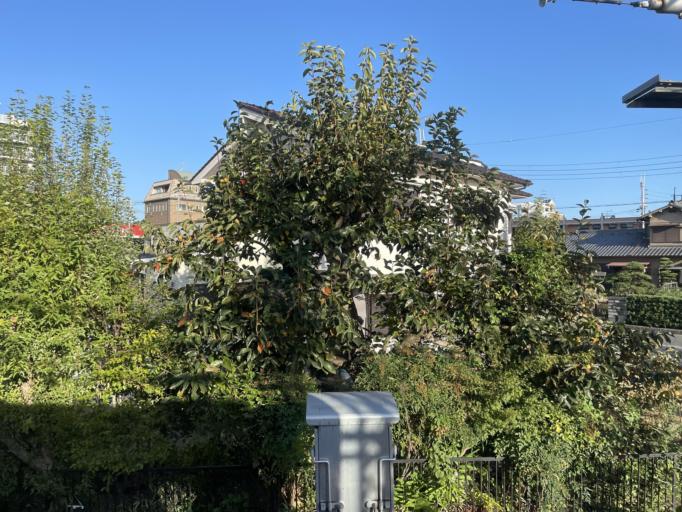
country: JP
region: Osaka
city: Tondabayashicho
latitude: 34.5055
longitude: 135.6027
